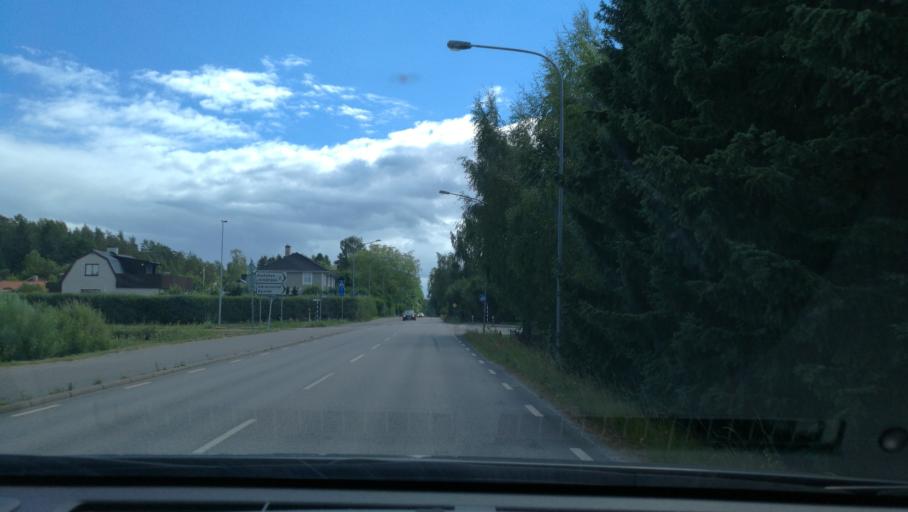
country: SE
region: OEstergoetland
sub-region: Norrkopings Kommun
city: Krokek
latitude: 58.6696
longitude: 16.3673
